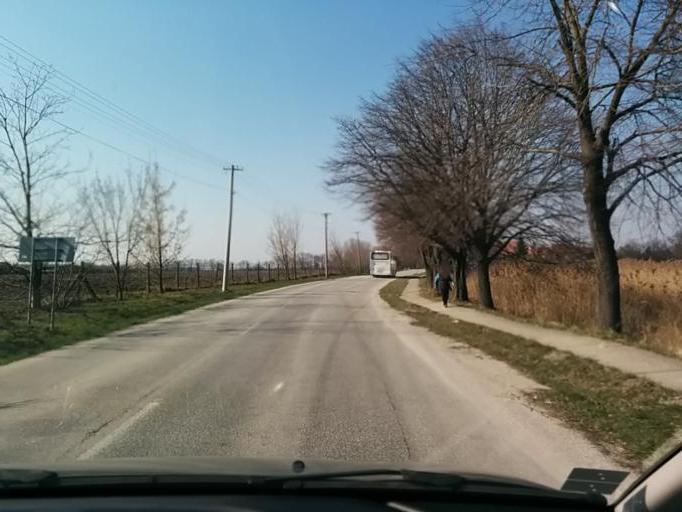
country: SK
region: Trnavsky
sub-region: Okres Galanta
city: Galanta
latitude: 48.2220
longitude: 17.7260
